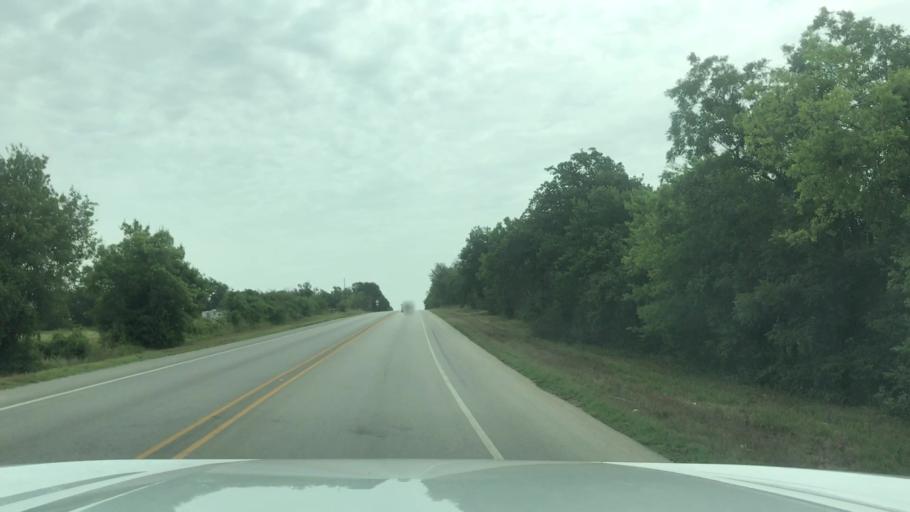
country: US
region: Texas
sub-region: Erath County
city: Dublin
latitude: 32.0987
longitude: -98.3964
